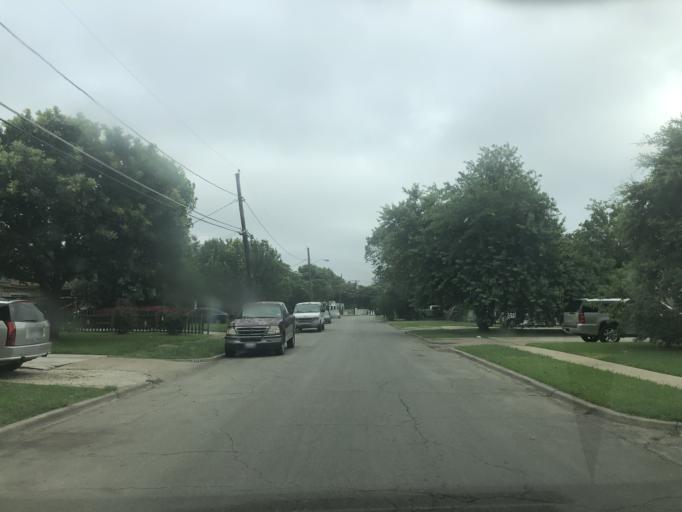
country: US
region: Texas
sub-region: Dallas County
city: Farmers Branch
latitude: 32.8644
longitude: -96.8718
